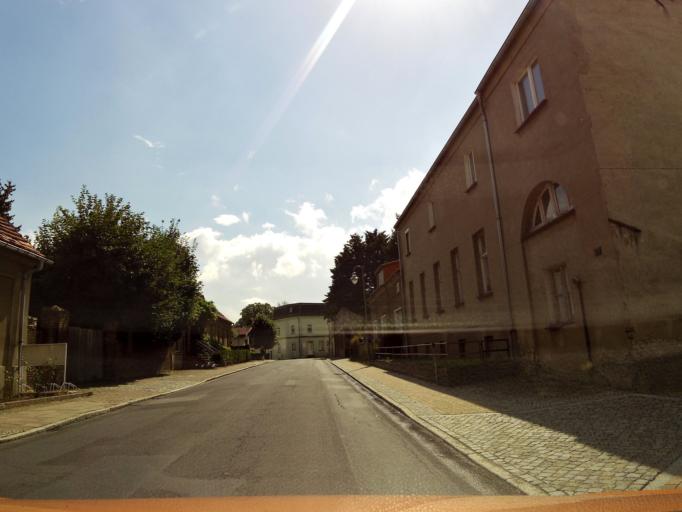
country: DE
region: Brandenburg
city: Ketzin
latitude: 52.4771
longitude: 12.8436
